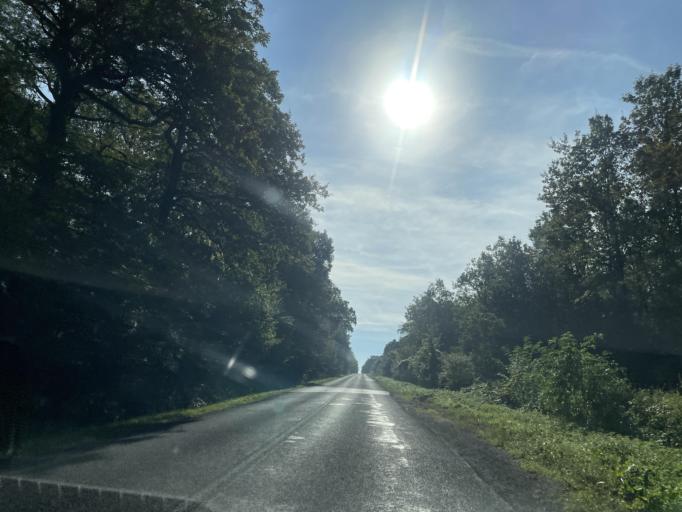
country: FR
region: Ile-de-France
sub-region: Departement de Seine-et-Marne
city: Trilport
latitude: 48.9568
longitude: 2.9848
